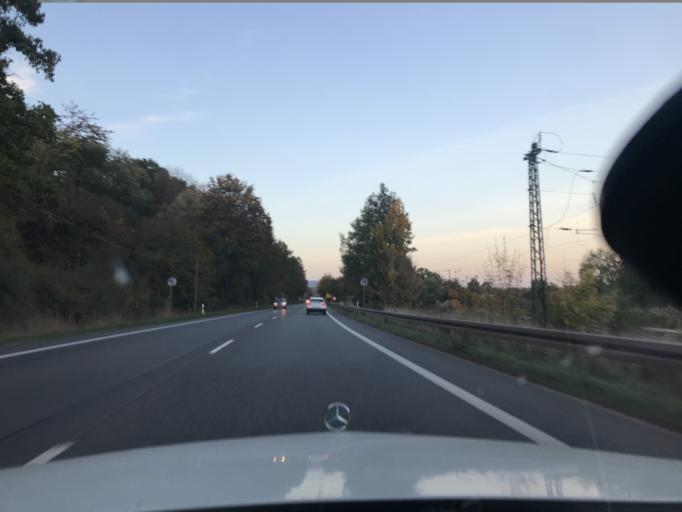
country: DE
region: Hesse
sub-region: Regierungsbezirk Kassel
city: Eschwege
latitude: 51.1507
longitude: 9.9818
